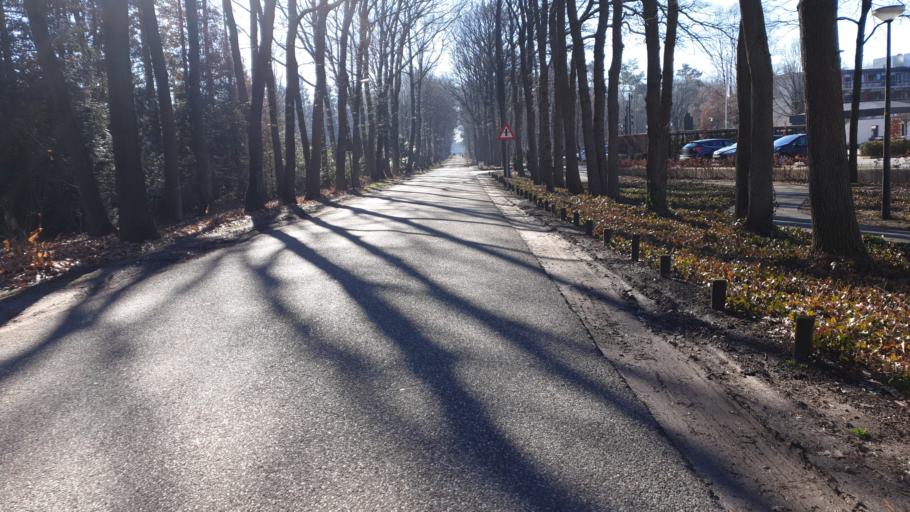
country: NL
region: Gelderland
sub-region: Gemeente Apeldoorn
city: Beekbergen
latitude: 52.1808
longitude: 5.9502
